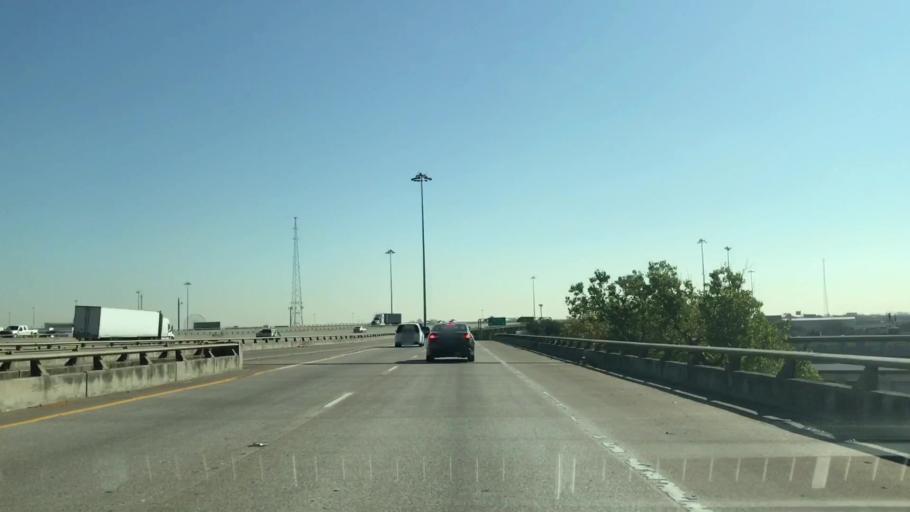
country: US
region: Texas
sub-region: Dallas County
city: Dallas
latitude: 32.7815
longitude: -96.7860
